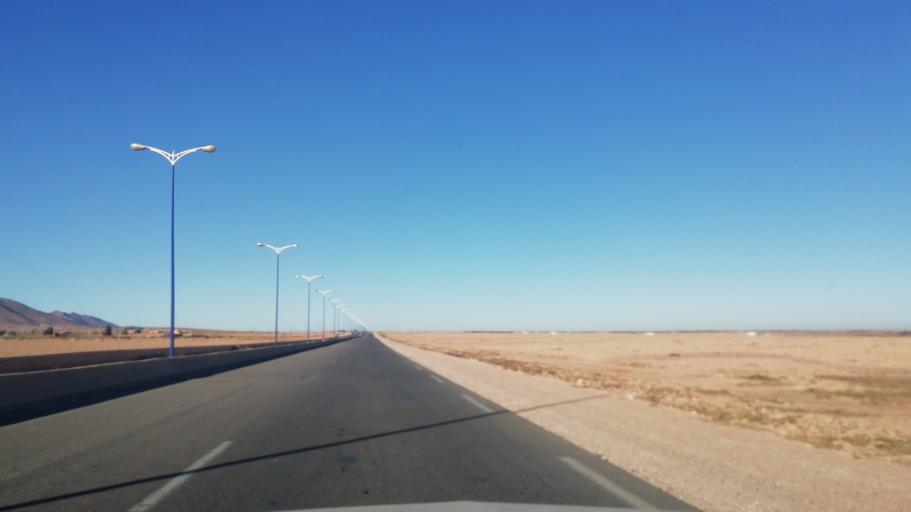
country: DZ
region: Wilaya de Naama
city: Naama
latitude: 33.5710
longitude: -0.2405
